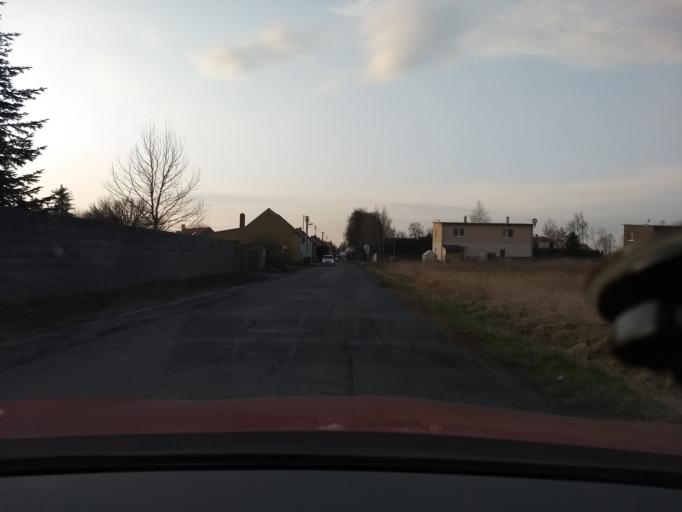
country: CZ
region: Central Bohemia
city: Jenec
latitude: 50.0485
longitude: 14.1810
